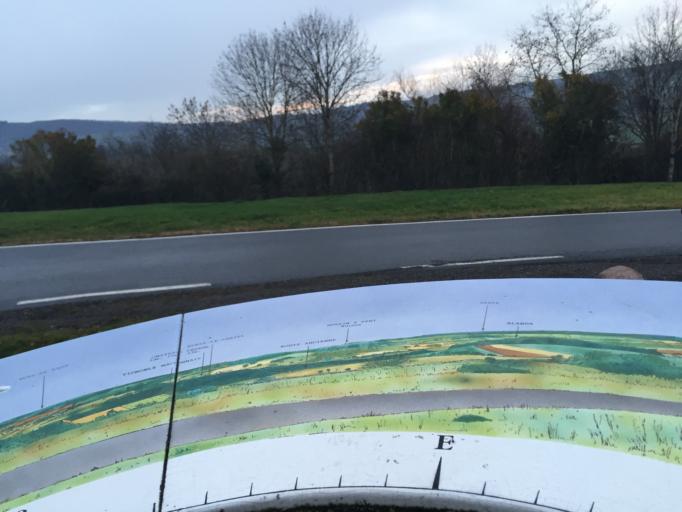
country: FR
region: Bourgogne
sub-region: Departement de Saone-et-Loire
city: Cluny
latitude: 46.3794
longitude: 4.6710
